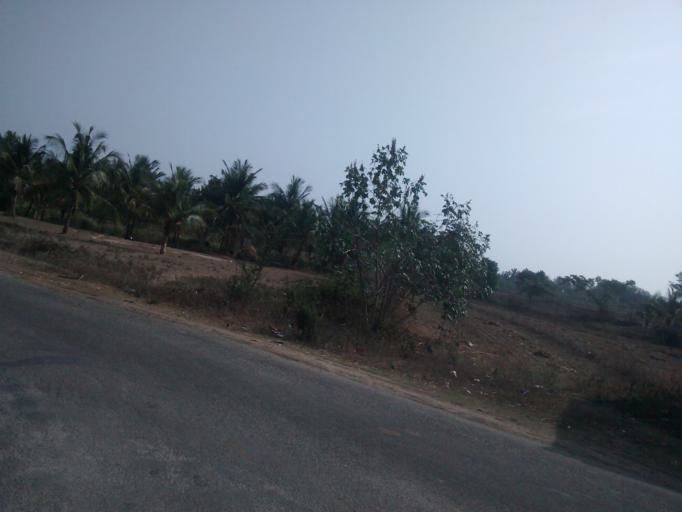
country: IN
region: Karnataka
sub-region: Hassan
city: Hassan
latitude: 12.9403
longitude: 76.1646
